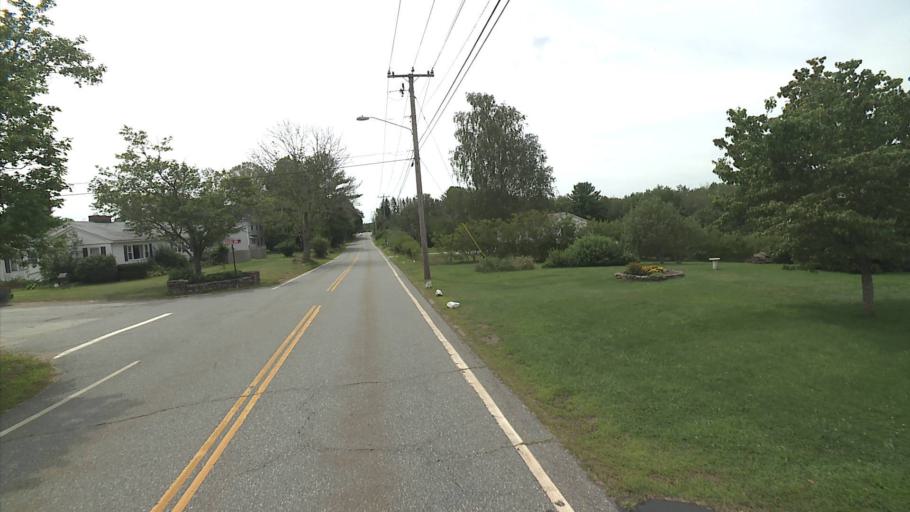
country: US
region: Connecticut
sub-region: Windham County
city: Thompson
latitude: 41.9974
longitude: -71.8450
